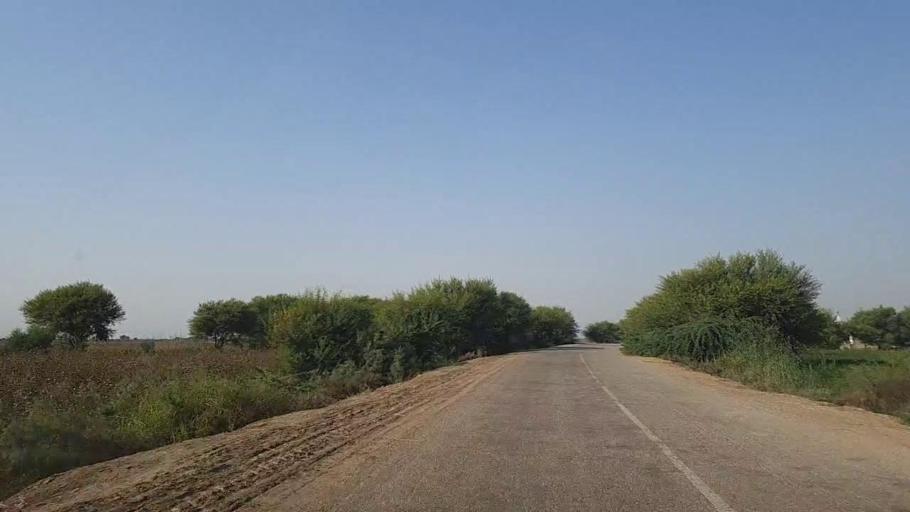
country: PK
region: Sindh
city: Mirpur Batoro
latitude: 24.5789
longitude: 68.3946
